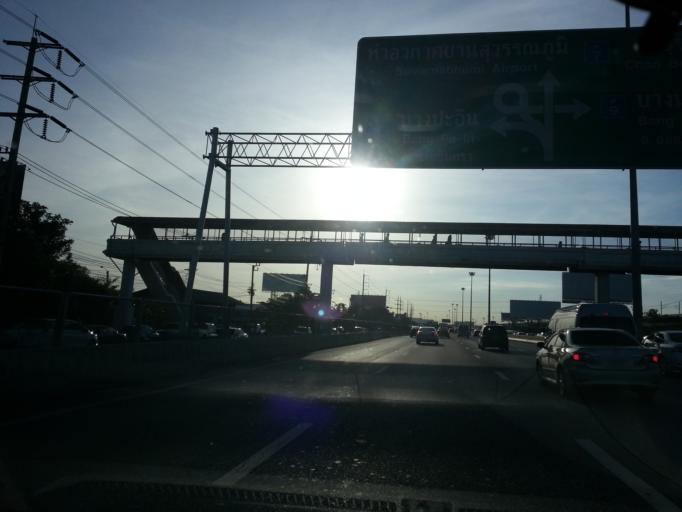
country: TH
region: Bangkok
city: Saphan Sung
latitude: 13.7340
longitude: 100.6912
